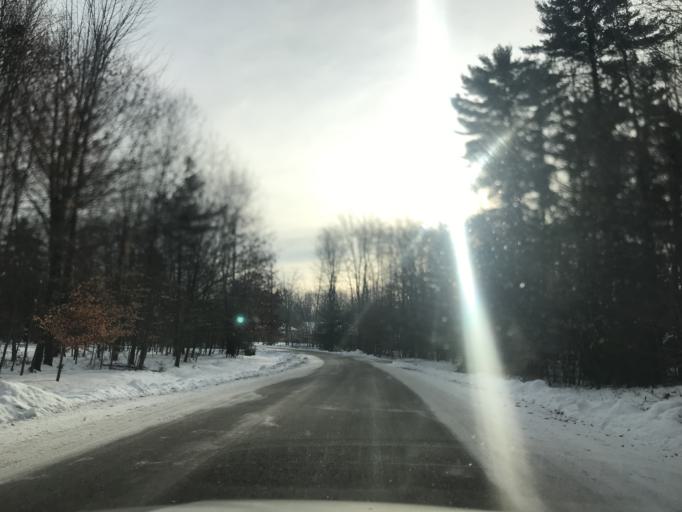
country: US
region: Wisconsin
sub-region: Brown County
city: Suamico
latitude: 44.6864
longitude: -88.0615
